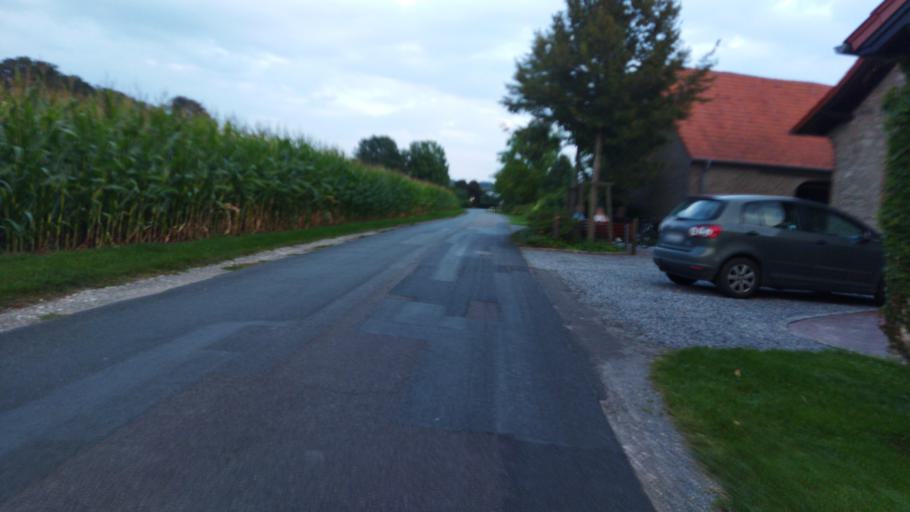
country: DE
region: Lower Saxony
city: Bad Laer
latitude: 52.1097
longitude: 8.0741
